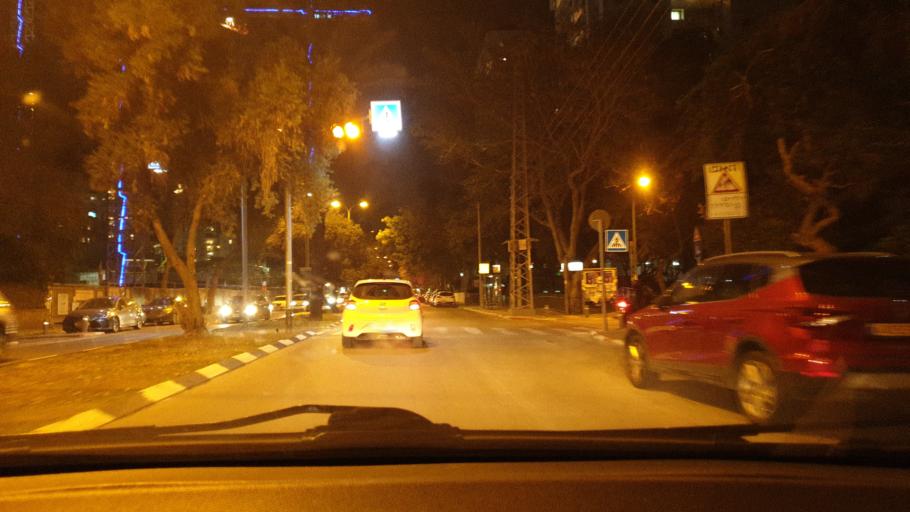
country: IL
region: Tel Aviv
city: Ramat Gan
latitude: 32.1225
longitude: 34.8025
